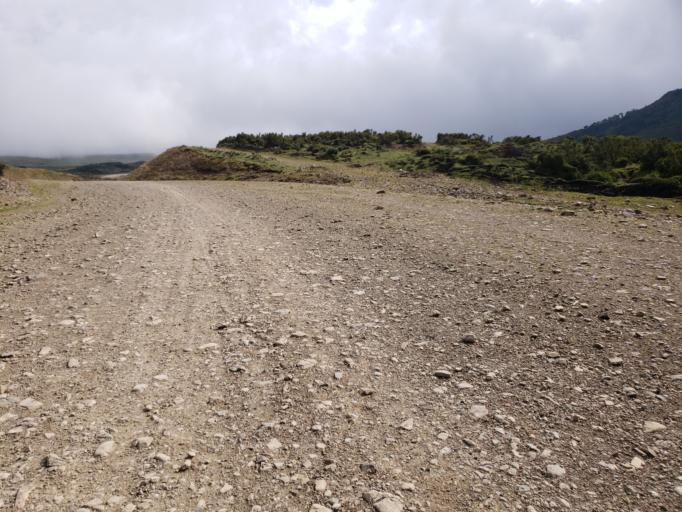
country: ET
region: Oromiya
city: Dodola
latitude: 6.7496
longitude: 39.4278
